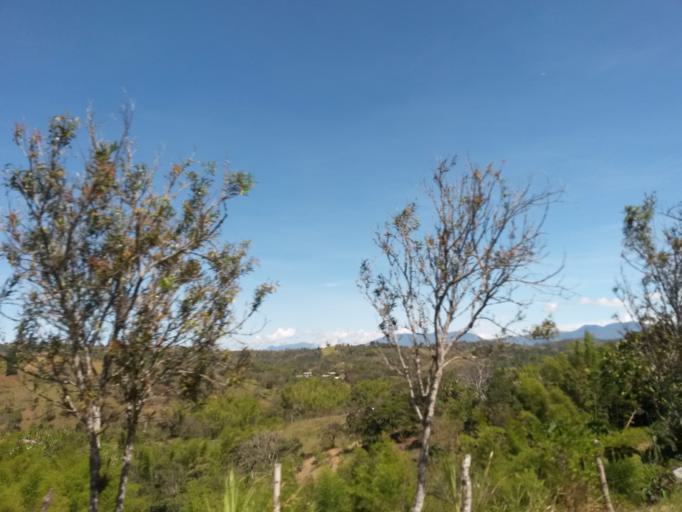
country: CO
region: Cauca
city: Lopez
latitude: 2.4336
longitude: -76.7693
